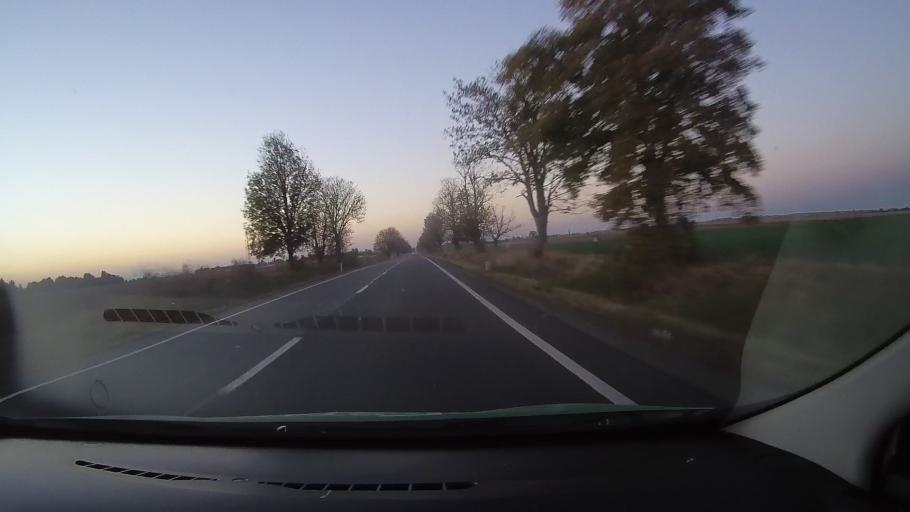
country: RO
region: Bihor
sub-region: Comuna Valea lui Mihai
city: Valea lui Mihai
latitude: 47.4950
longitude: 22.1521
